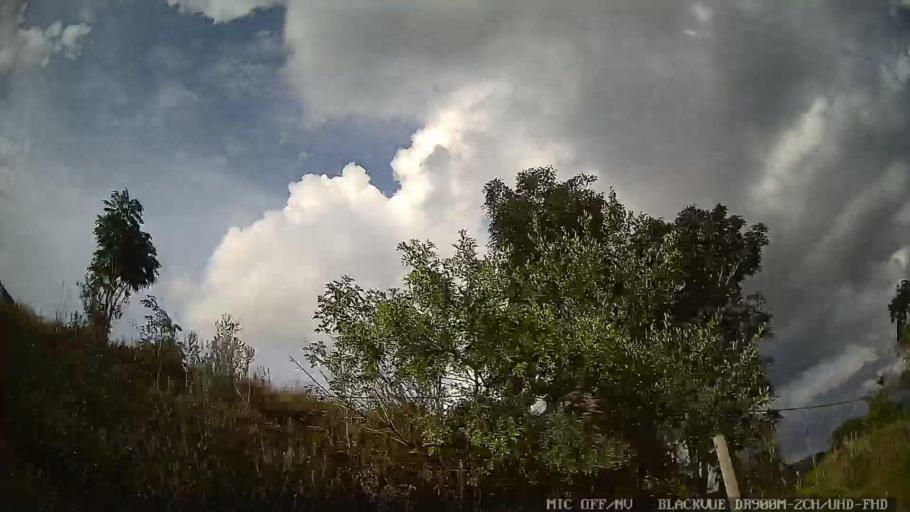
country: BR
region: Sao Paulo
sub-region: Braganca Paulista
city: Braganca Paulista
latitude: -22.9113
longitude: -46.4678
